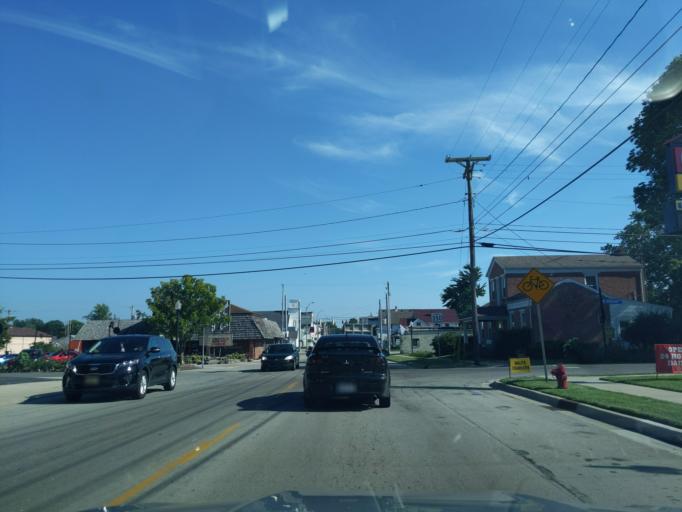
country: US
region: Indiana
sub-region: Ripley County
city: Osgood
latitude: 39.1331
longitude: -85.2929
